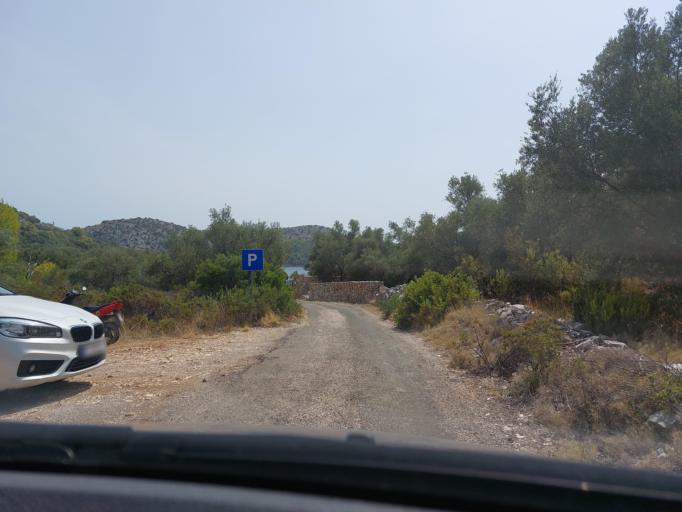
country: HR
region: Dubrovacko-Neretvanska
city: Smokvica
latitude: 42.7381
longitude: 16.8874
